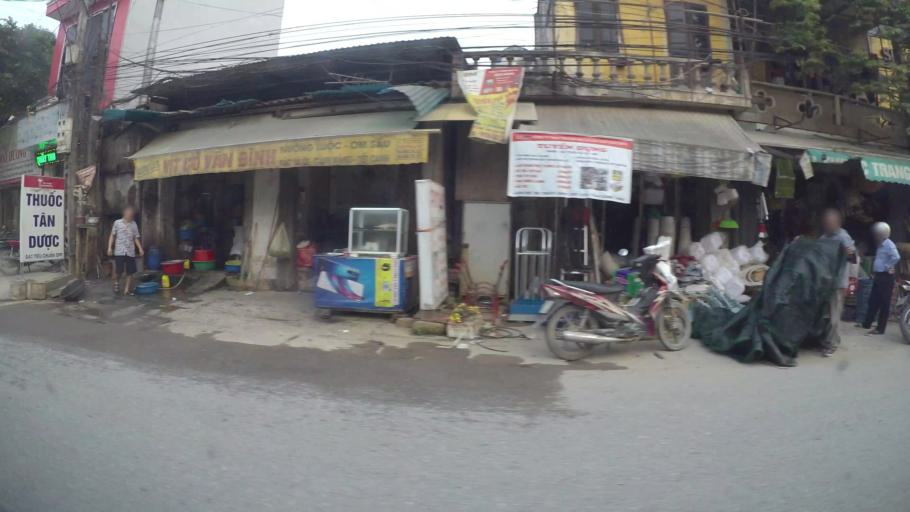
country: VN
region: Ha Noi
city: Ha Dong
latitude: 20.9915
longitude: 105.7289
